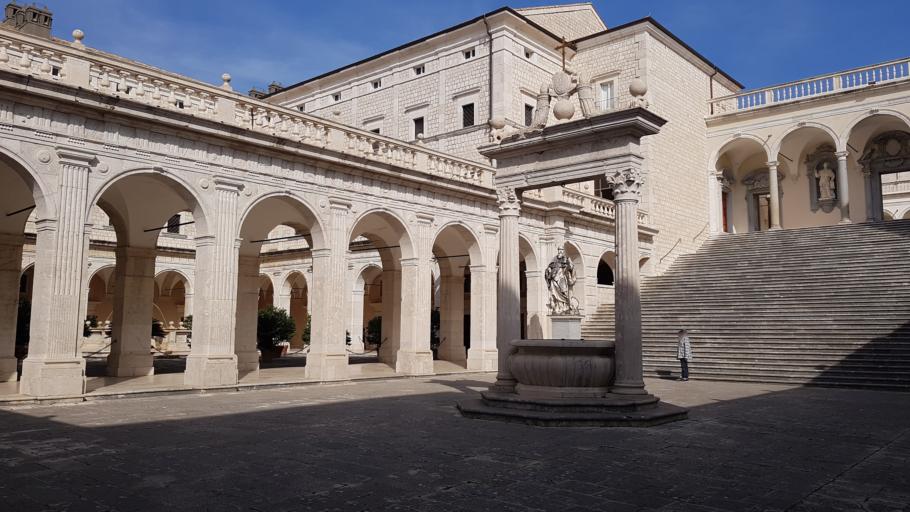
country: IT
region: Latium
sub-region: Provincia di Frosinone
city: Cassino
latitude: 41.4908
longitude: 13.8130
